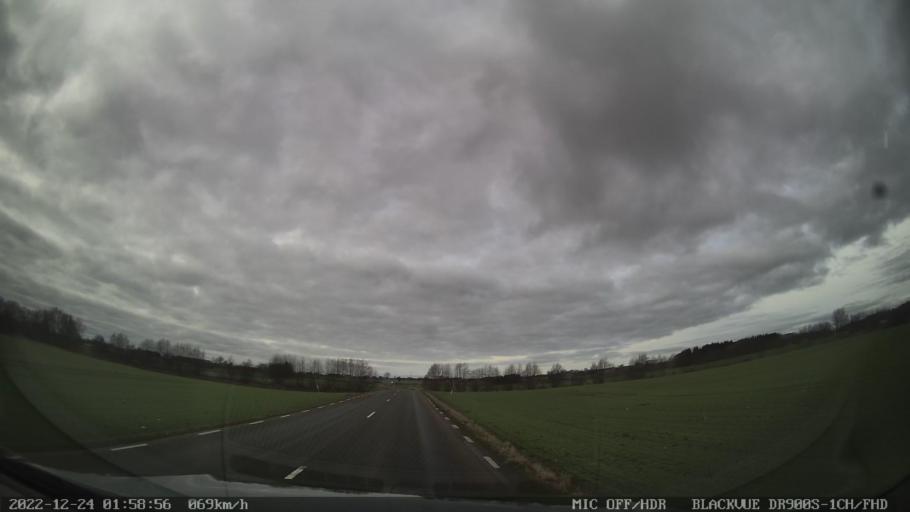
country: SE
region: Skane
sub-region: Tomelilla Kommun
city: Tomelilla
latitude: 55.6058
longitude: 14.0241
